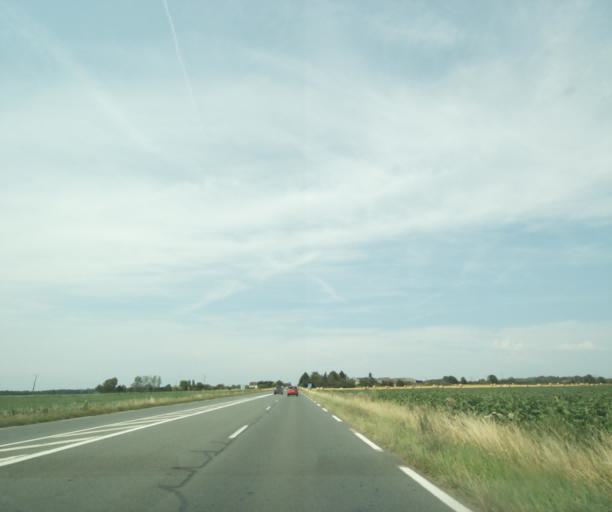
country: FR
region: Centre
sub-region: Departement d'Indre-et-Loire
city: Sorigny
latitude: 47.2026
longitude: 0.6720
